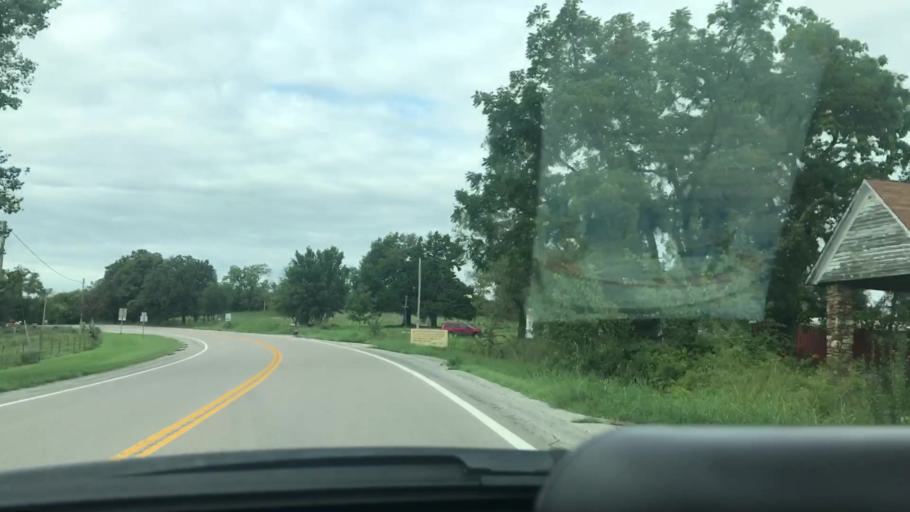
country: US
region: Missouri
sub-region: Benton County
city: Warsaw
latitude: 38.1180
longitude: -93.2758
